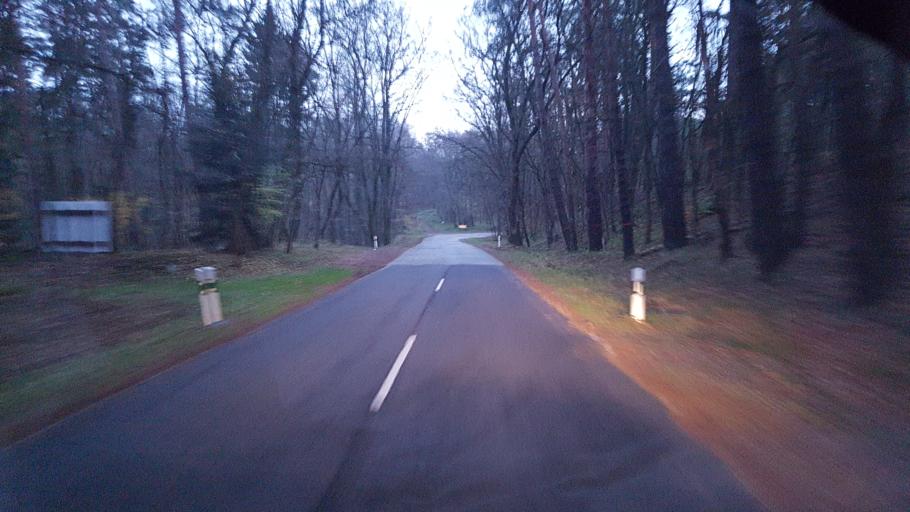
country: DE
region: Brandenburg
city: Jamlitz
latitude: 51.9983
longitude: 14.3698
